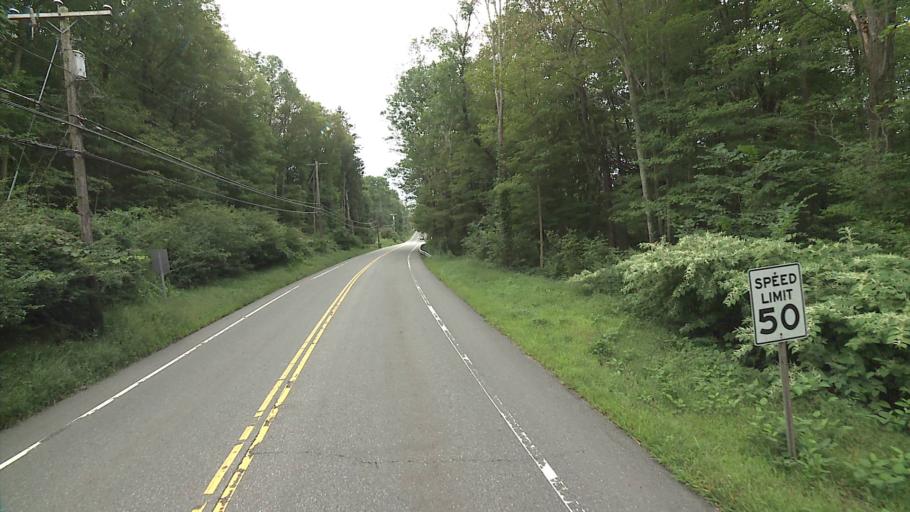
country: US
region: Connecticut
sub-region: Tolland County
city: Hebron
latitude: 41.6237
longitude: -72.3429
